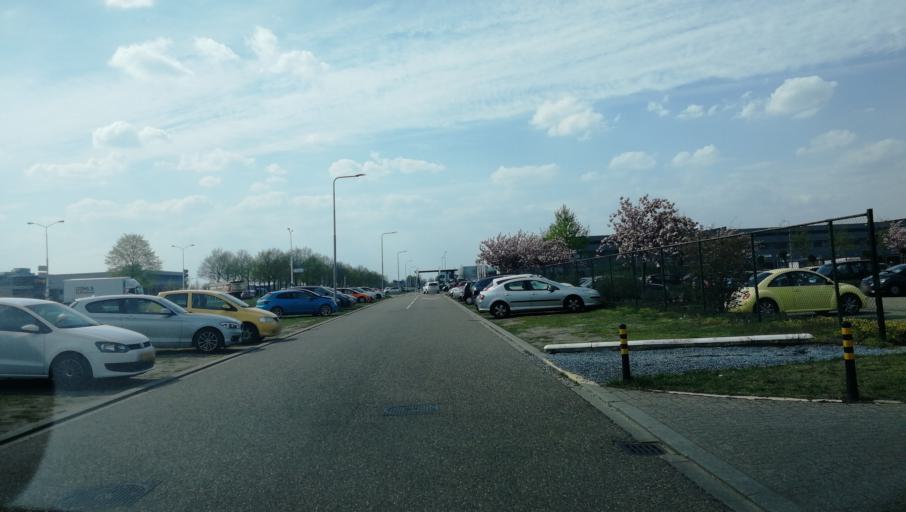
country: NL
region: Limburg
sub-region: Gemeente Peel en Maas
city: Maasbree
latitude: 51.3990
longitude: 6.0797
